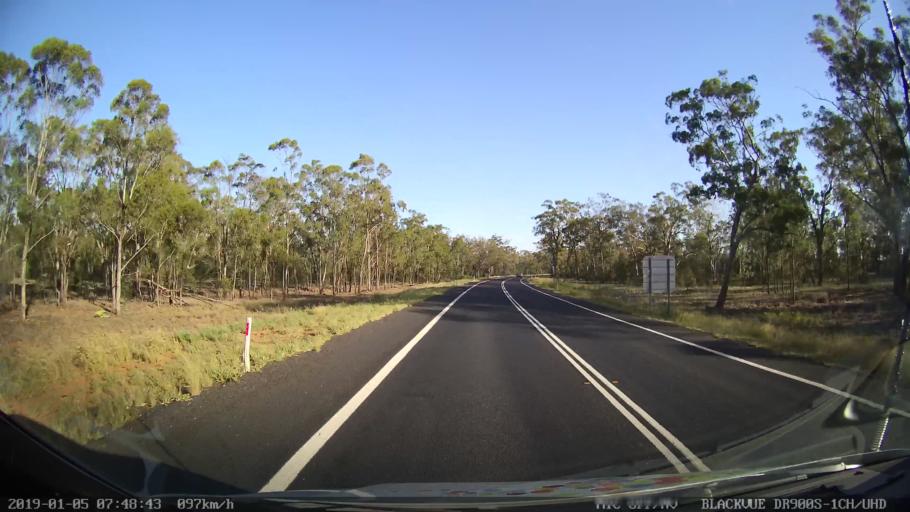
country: AU
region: New South Wales
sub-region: Gilgandra
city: Gilgandra
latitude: -31.8124
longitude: 148.6367
